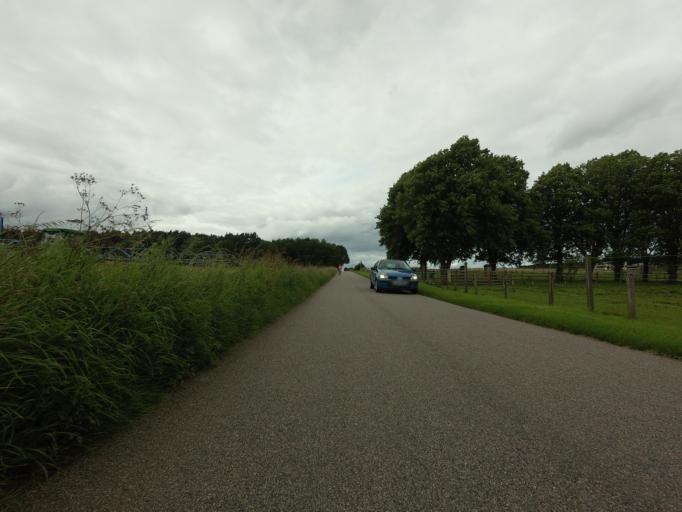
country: GB
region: Scotland
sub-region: Moray
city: Forres
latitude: 57.6011
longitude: -3.7228
